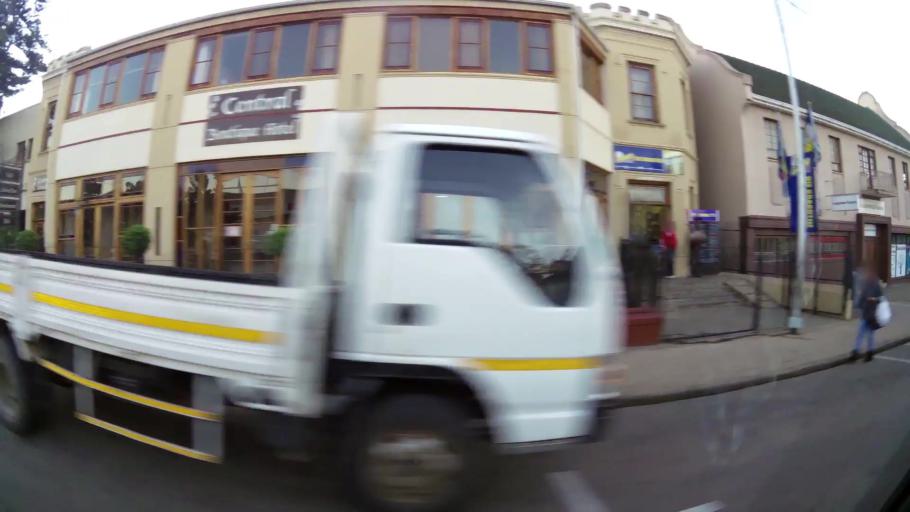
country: ZA
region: Western Cape
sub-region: Eden District Municipality
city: Riversdale
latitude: -34.0920
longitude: 21.2609
